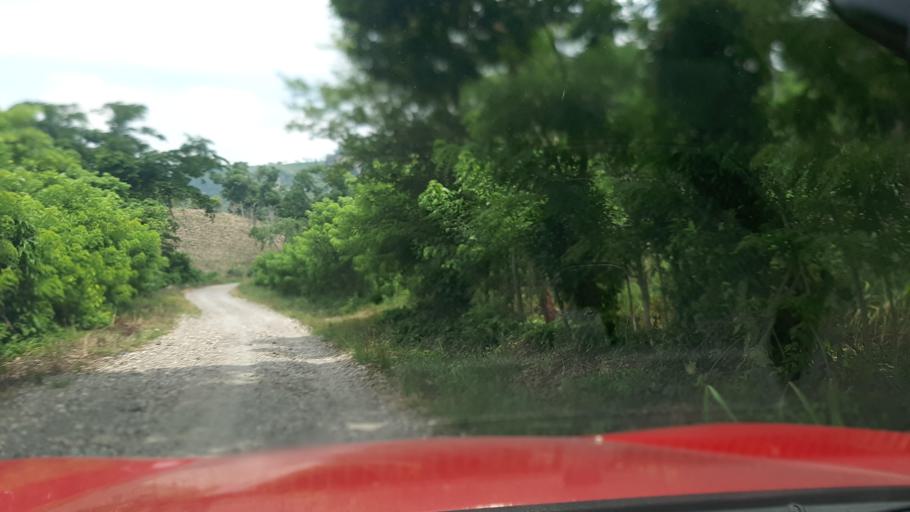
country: MX
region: Veracruz
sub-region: Papantla
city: Polutla
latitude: 20.4614
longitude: -97.1855
